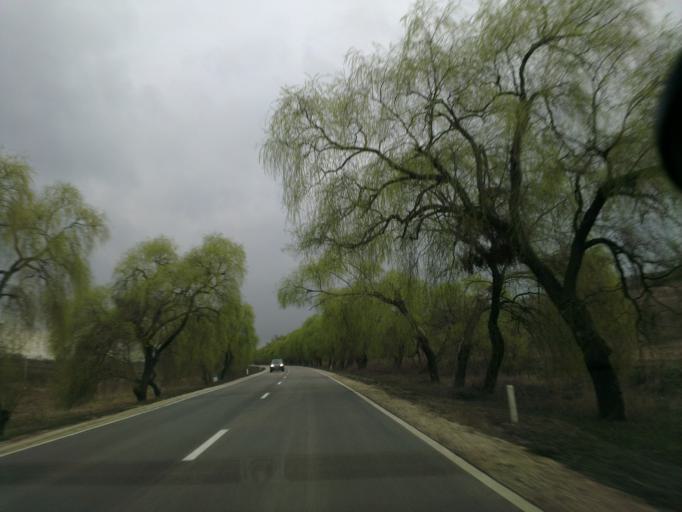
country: MD
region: Hincesti
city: Hincesti
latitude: 46.8333
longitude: 28.6160
